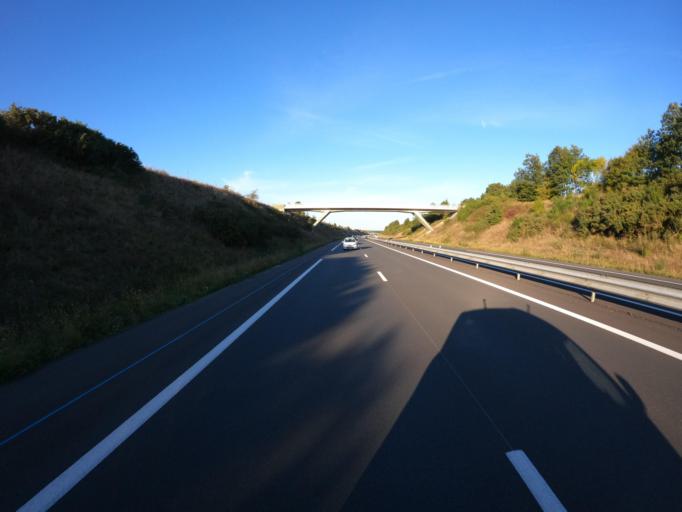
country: FR
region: Pays de la Loire
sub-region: Departement de la Vendee
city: Saint-Fulgent
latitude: 46.8287
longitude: -1.1698
